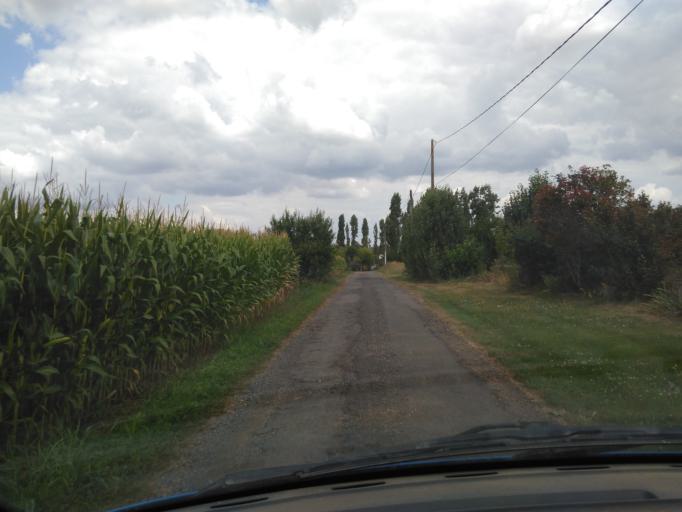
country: FR
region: Pays de la Loire
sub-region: Departement de la Vendee
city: Sainte-Hermine
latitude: 46.5548
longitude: -1.0275
